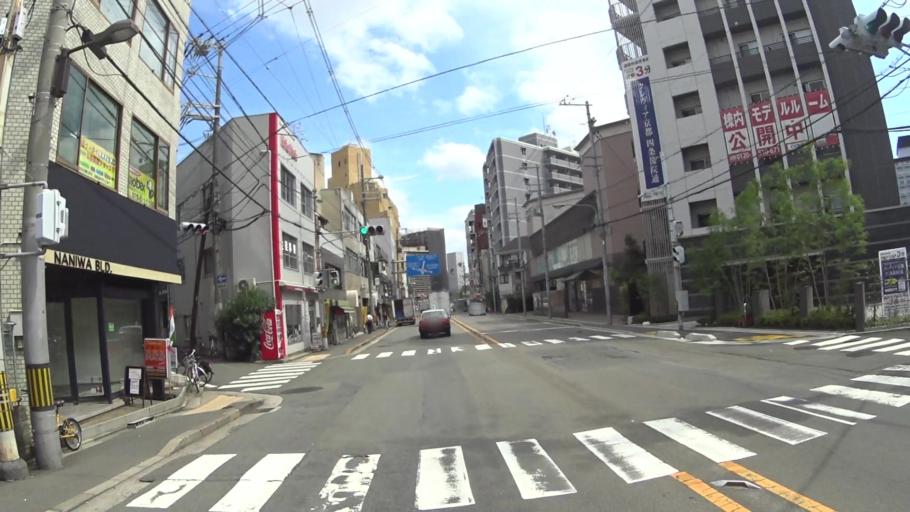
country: JP
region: Kyoto
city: Kyoto
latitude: 35.0052
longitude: 135.7472
